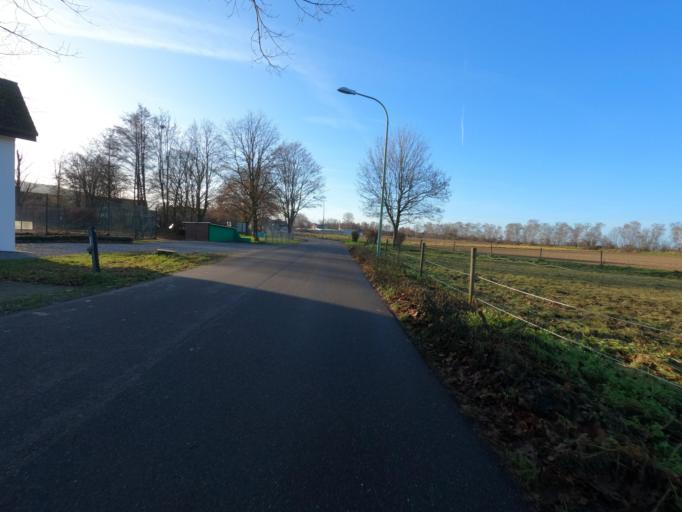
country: DE
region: North Rhine-Westphalia
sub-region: Regierungsbezirk Koln
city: Titz
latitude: 50.9564
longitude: 6.4281
